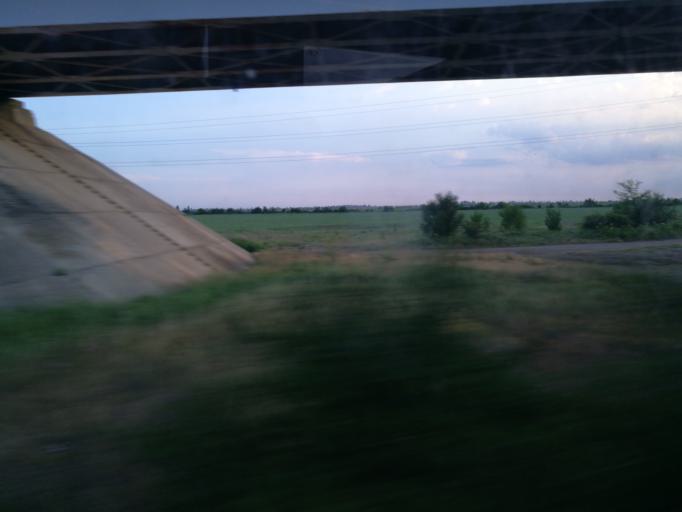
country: RO
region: Dambovita
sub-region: Comuna Contesti
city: Balteni
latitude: 44.6471
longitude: 25.6983
